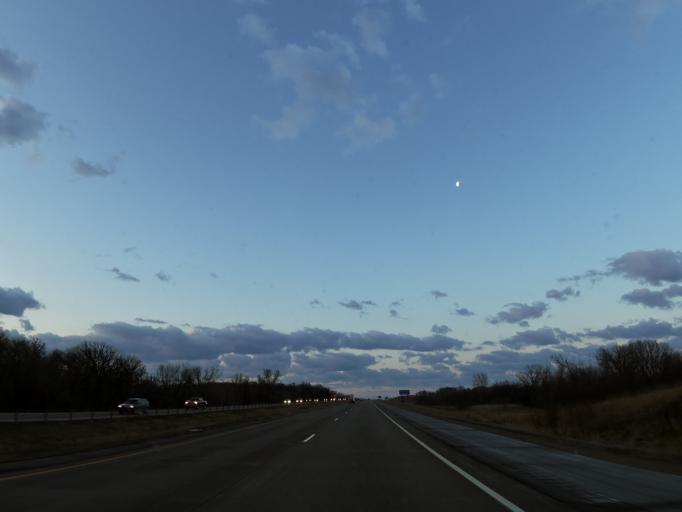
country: US
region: Minnesota
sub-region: Scott County
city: Elko New Market
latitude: 44.5864
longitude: -93.2979
